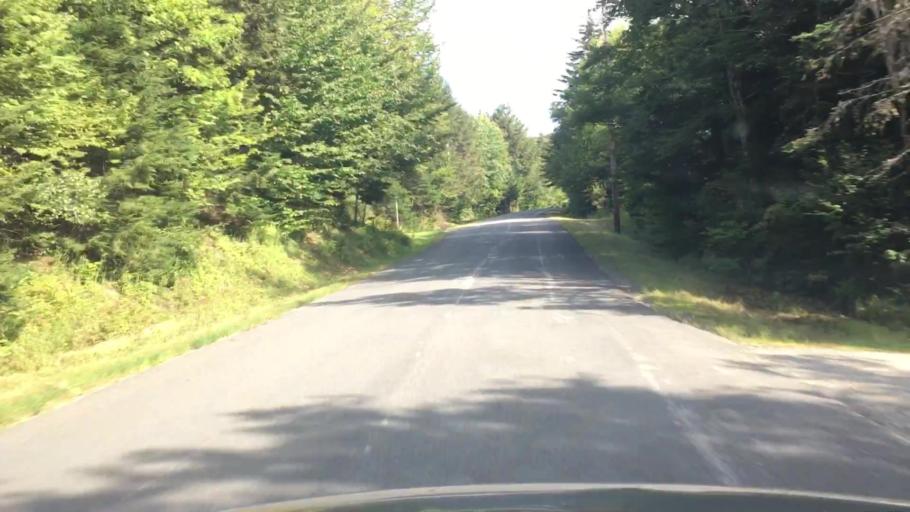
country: US
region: Vermont
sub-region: Windham County
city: Dover
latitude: 42.8473
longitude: -72.8334
